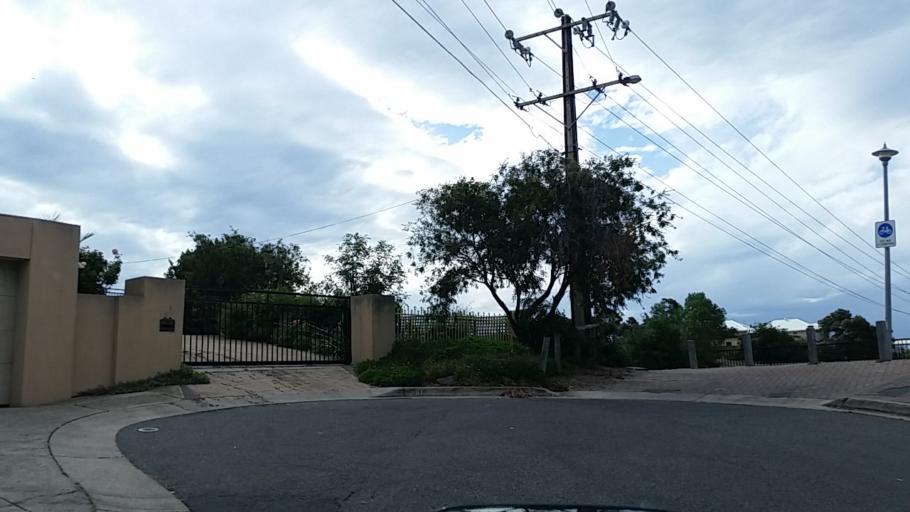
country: AU
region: South Australia
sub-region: Charles Sturt
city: Henley Beach
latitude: -34.9353
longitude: 138.5005
